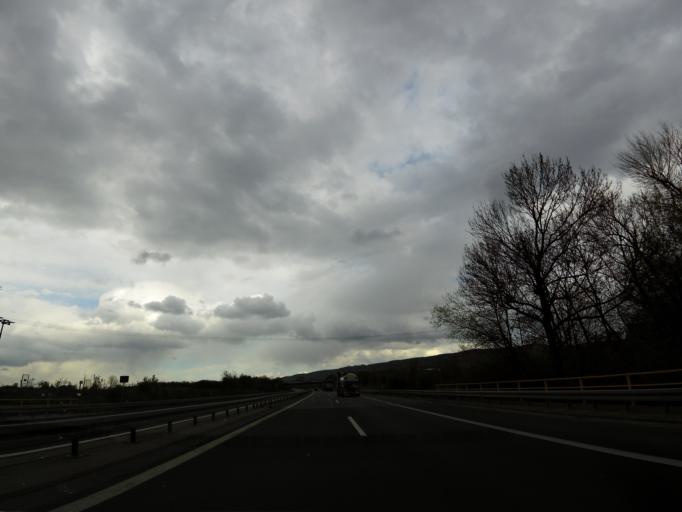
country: DE
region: Saxony-Anhalt
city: Wernigerode
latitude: 51.8559
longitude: 10.8065
